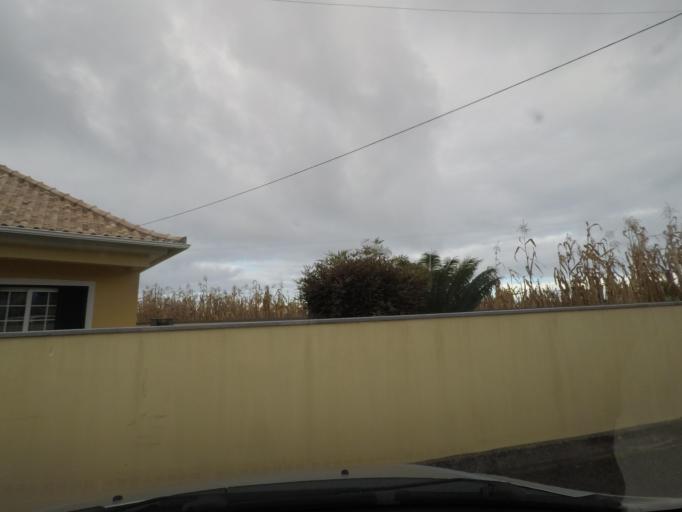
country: PT
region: Madeira
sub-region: Santana
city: Santana
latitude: 32.8158
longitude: -16.8791
